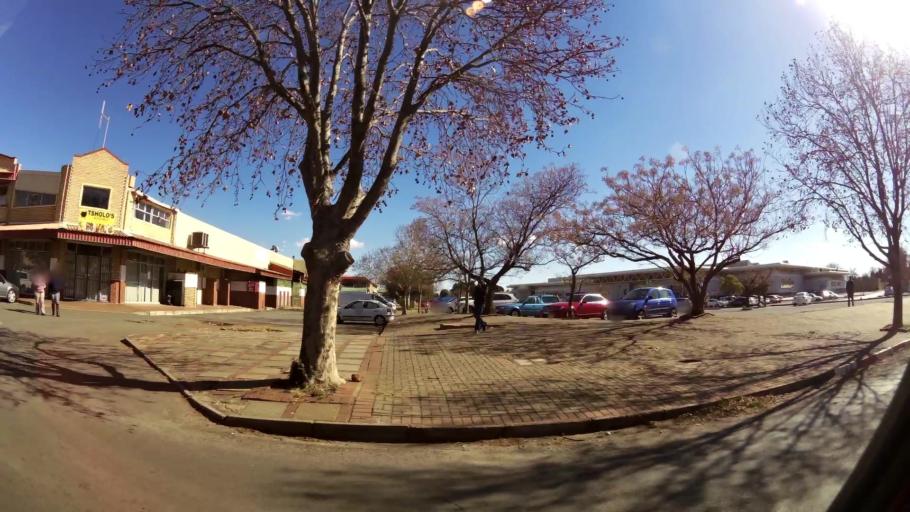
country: ZA
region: Gauteng
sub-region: West Rand District Municipality
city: Carletonville
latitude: -26.3579
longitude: 27.3965
